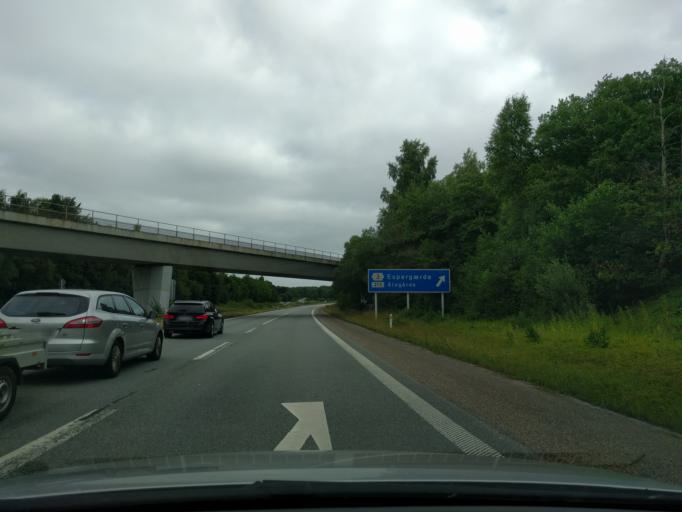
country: DK
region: Capital Region
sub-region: Fredensborg Kommune
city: Humlebaek
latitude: 55.9990
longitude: 12.5209
